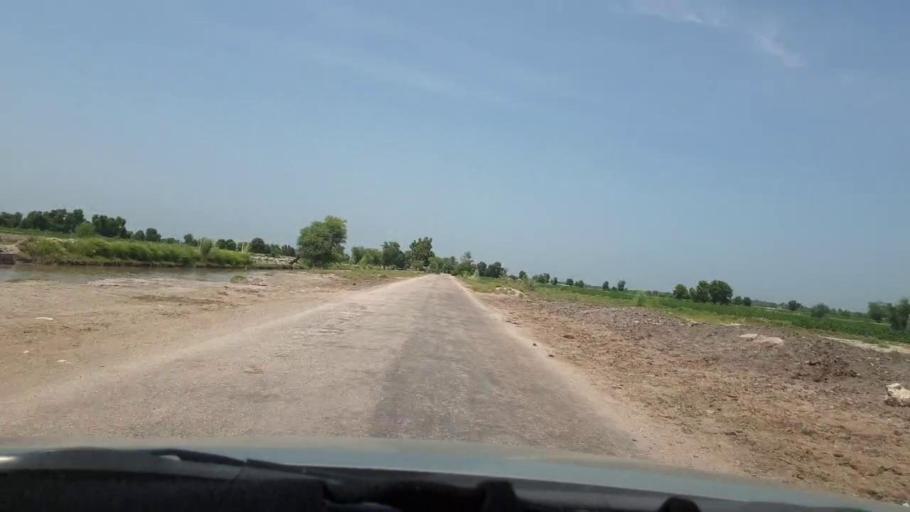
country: PK
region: Sindh
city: Pano Aqil
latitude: 27.6655
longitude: 69.1080
